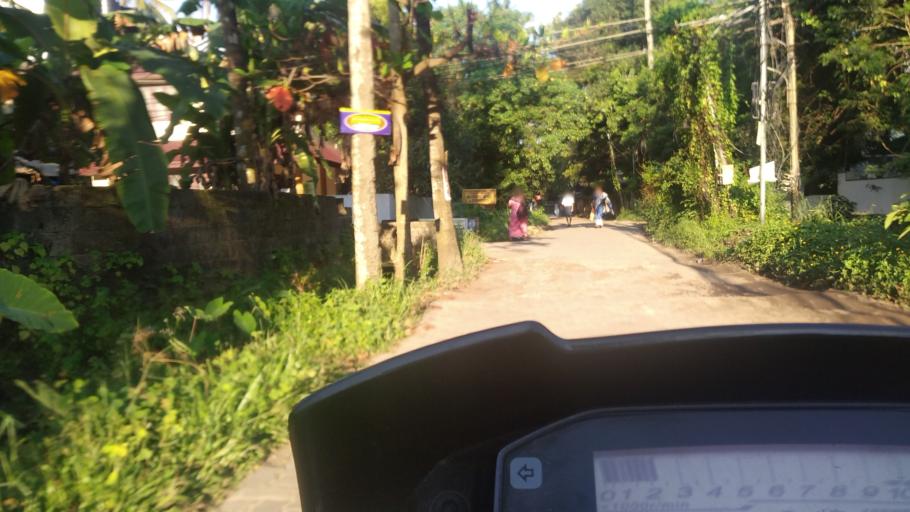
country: IN
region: Kerala
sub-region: Ernakulam
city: Cochin
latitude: 9.9447
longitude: 76.3243
